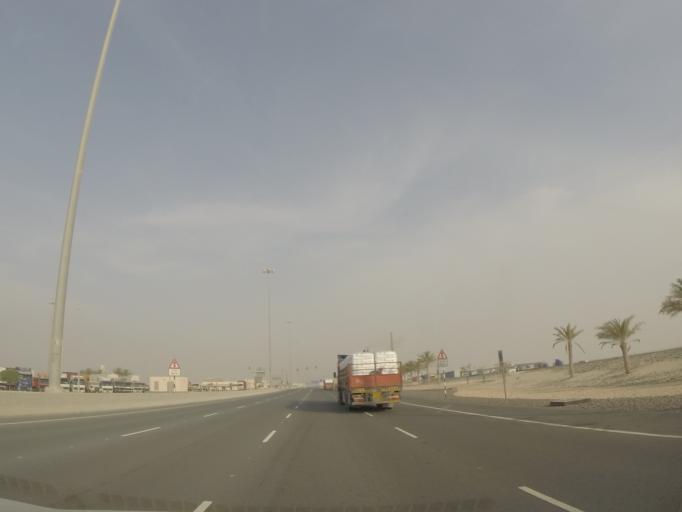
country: AE
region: Abu Dhabi
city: Abu Dhabi
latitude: 24.7787
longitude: 54.7076
